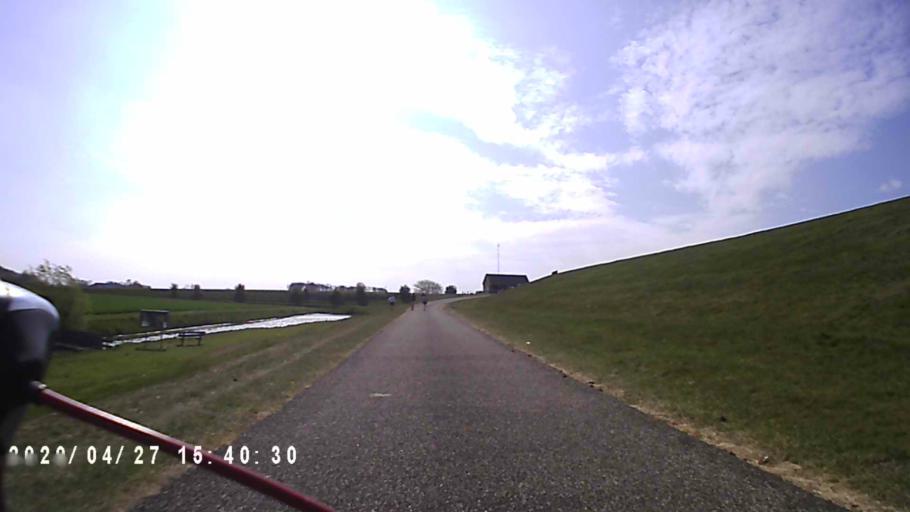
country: NL
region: Groningen
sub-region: Gemeente De Marne
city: Ulrum
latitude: 53.3924
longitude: 6.3089
